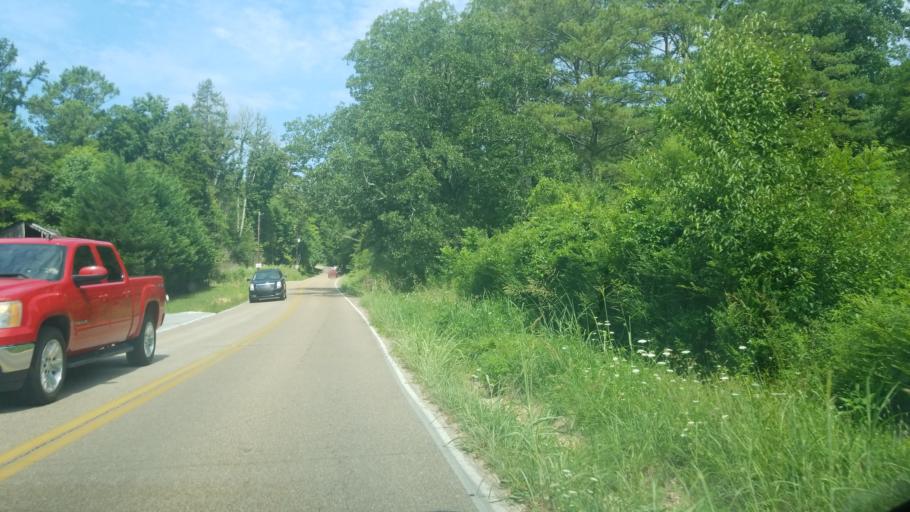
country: US
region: Tennessee
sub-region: Hamilton County
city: Lakesite
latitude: 35.1673
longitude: -85.0663
